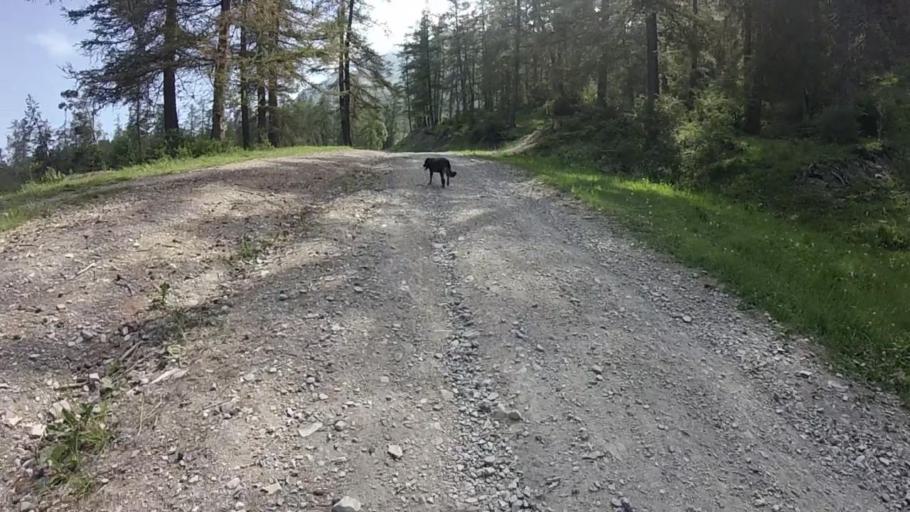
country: FR
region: Provence-Alpes-Cote d'Azur
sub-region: Departement des Alpes-de-Haute-Provence
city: Seyne-les-Alpes
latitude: 44.4042
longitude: 6.3648
